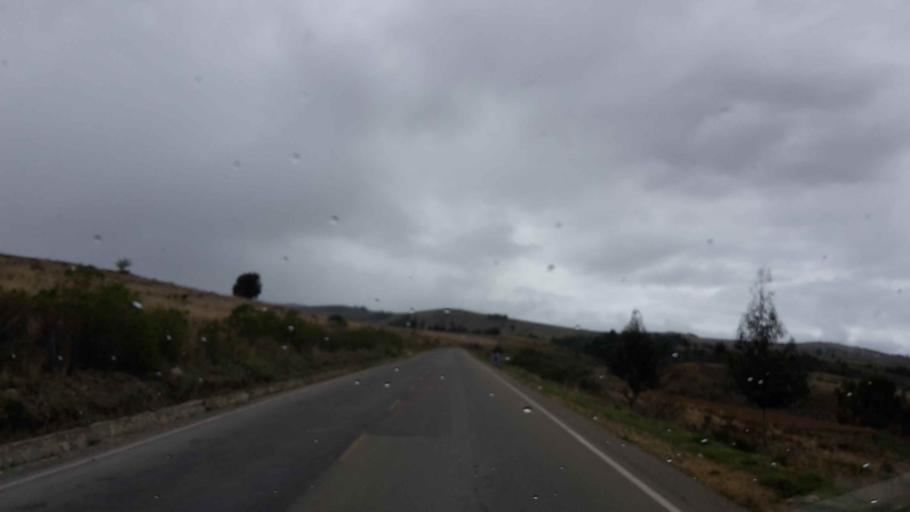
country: BO
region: Cochabamba
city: Arani
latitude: -17.4647
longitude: -65.6928
